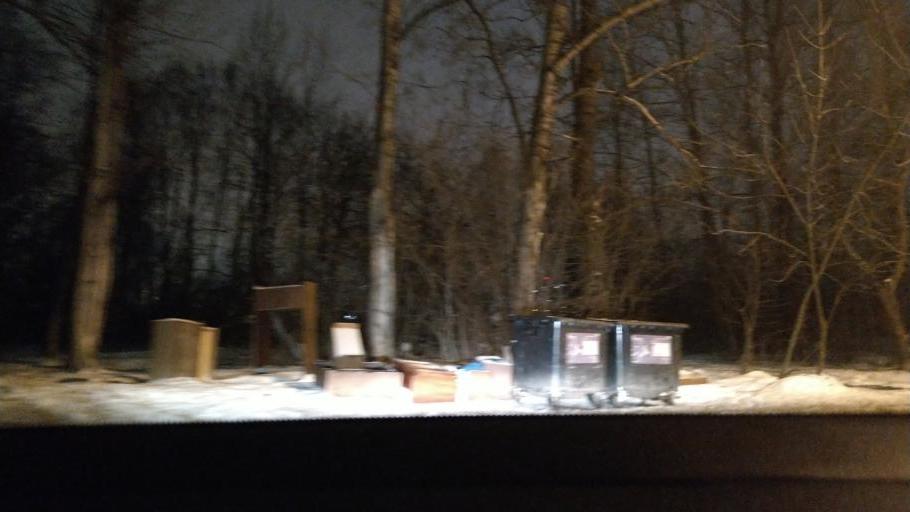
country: RU
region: Moskovskaya
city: Odintsovo
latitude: 55.6592
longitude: 37.2716
